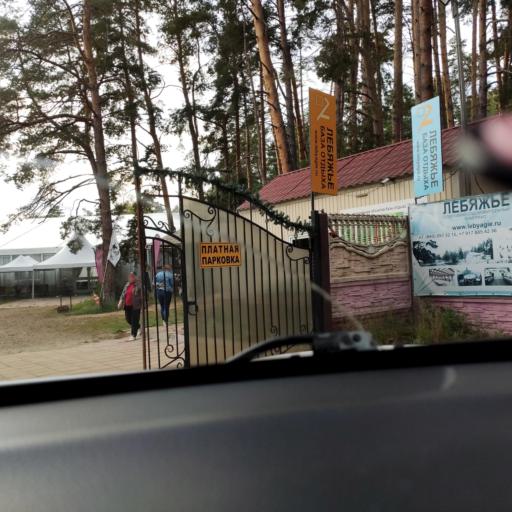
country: RU
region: Tatarstan
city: Staroye Arakchino
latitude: 55.8412
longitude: 48.9691
